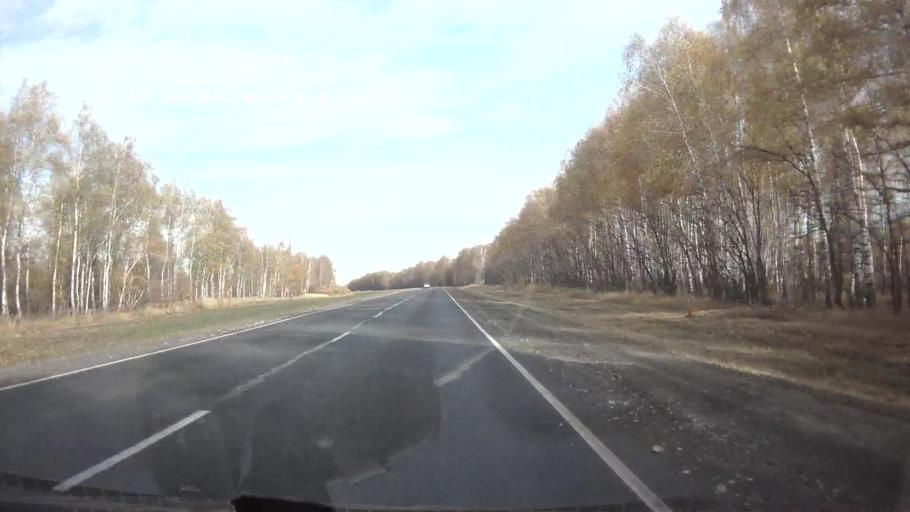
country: RU
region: Penza
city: Issa
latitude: 53.8177
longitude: 44.8387
